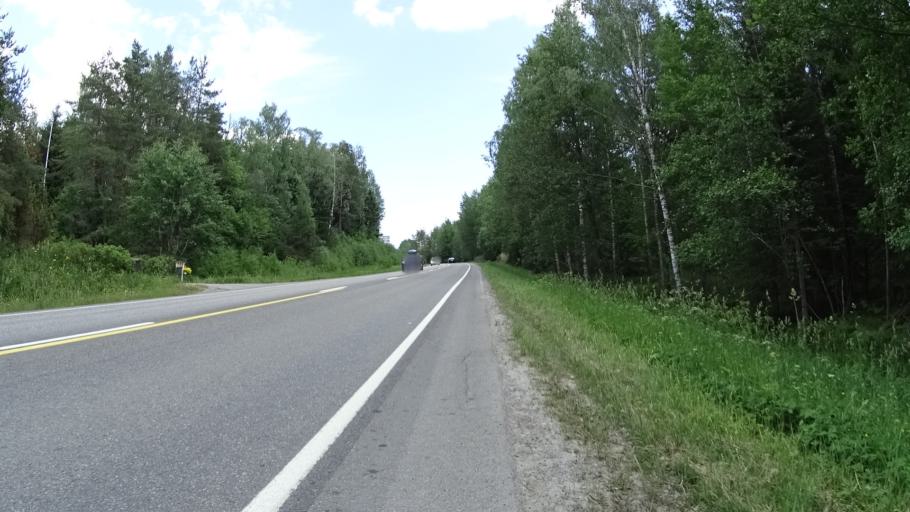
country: FI
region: Uusimaa
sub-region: Raaseporin
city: Pohja
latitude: 60.1037
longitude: 23.5658
